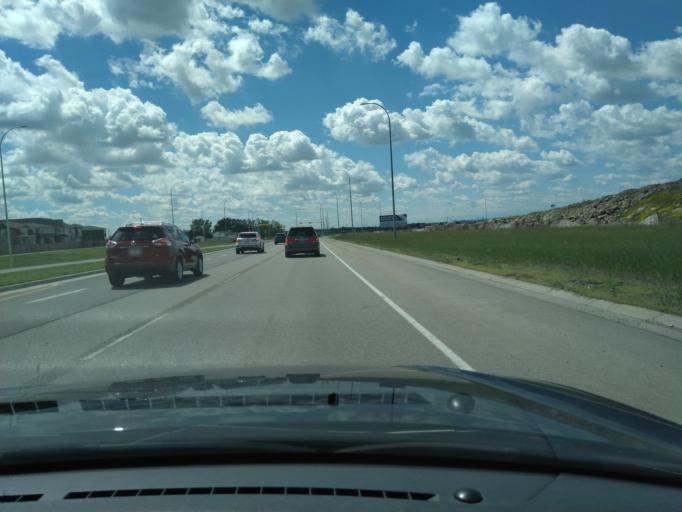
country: CA
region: Alberta
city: Calgary
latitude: 51.1347
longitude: -113.9703
